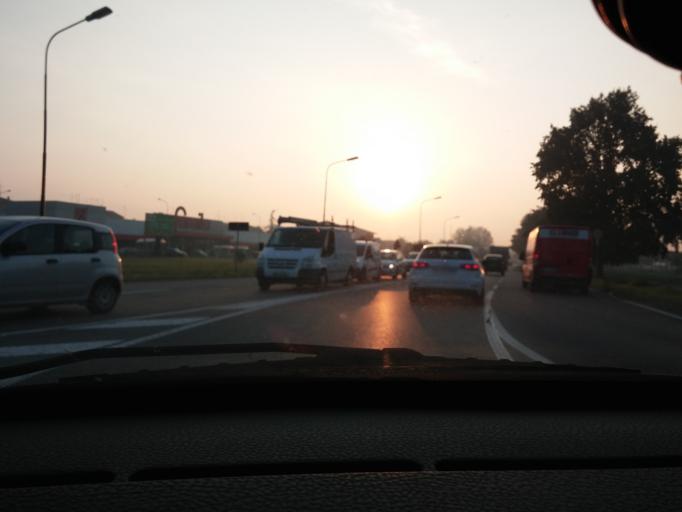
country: IT
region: Emilia-Romagna
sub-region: Provincia di Ferrara
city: Ferrara
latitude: 44.8188
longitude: 11.6038
